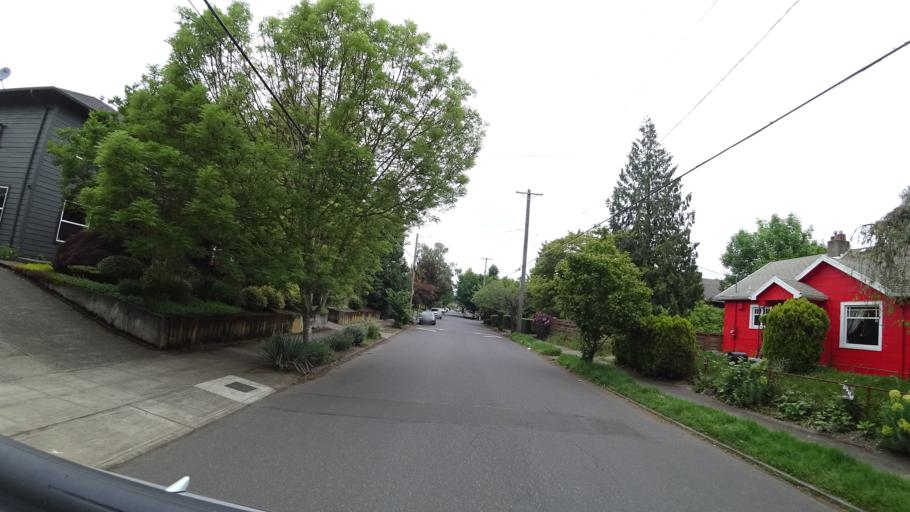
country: US
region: Oregon
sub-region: Multnomah County
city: Lents
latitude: 45.5208
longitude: -122.6076
